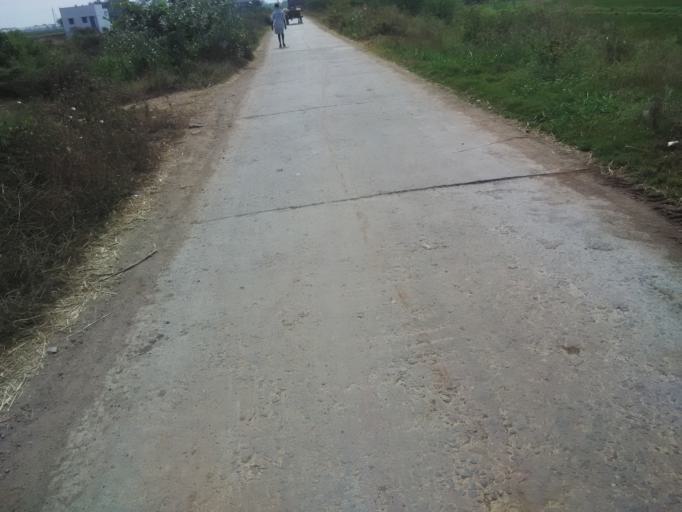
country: IN
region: Andhra Pradesh
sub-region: Kurnool
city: Nandyal
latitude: 15.4475
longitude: 78.4220
